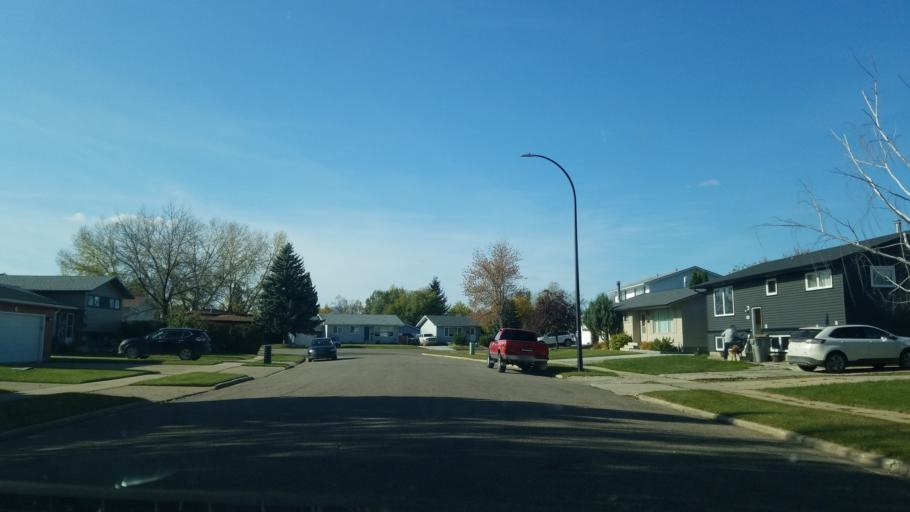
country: CA
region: Saskatchewan
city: Lloydminster
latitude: 53.2676
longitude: -110.0143
